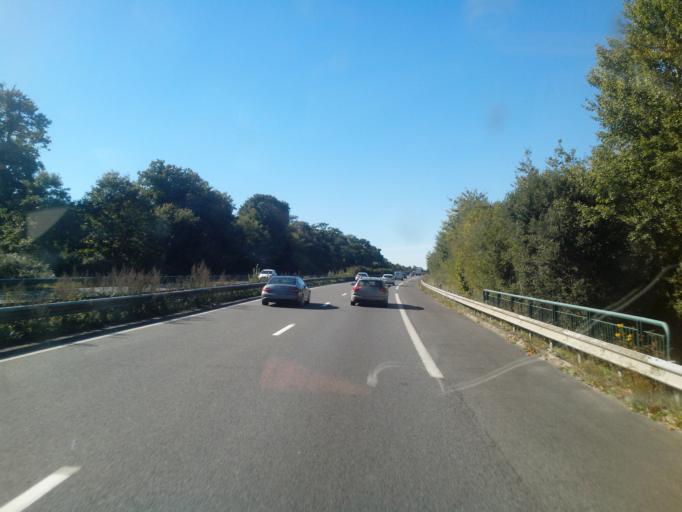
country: FR
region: Pays de la Loire
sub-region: Departement de la Loire-Atlantique
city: La Chapelle-des-Marais
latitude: 47.4866
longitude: -2.2204
